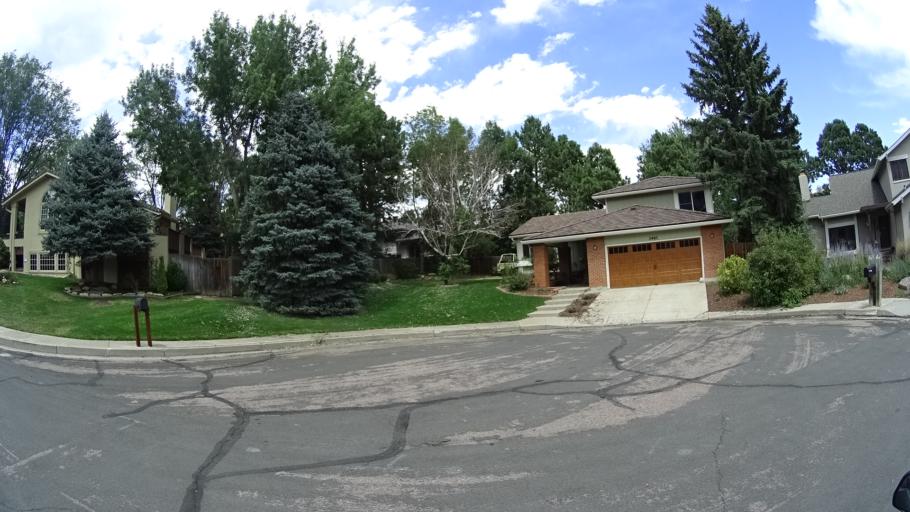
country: US
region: Colorado
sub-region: El Paso County
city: Stratmoor
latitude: 38.7816
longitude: -104.8288
